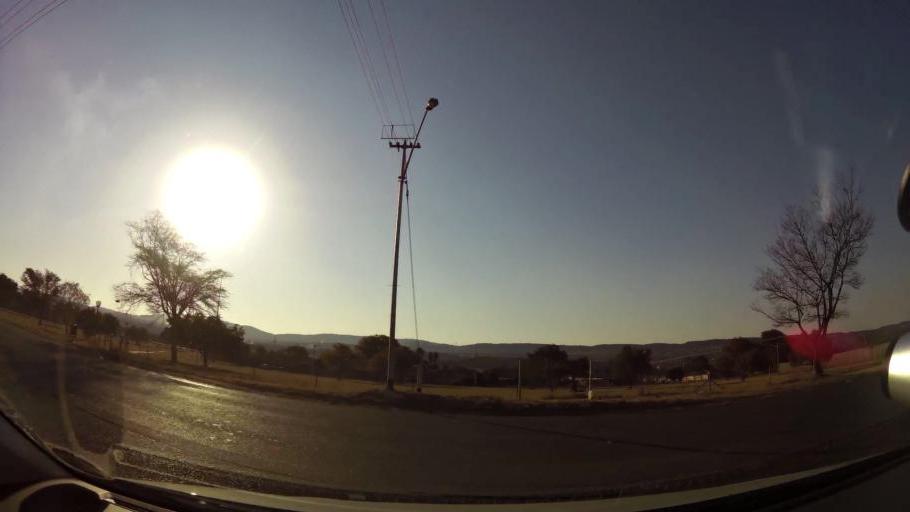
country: ZA
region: Gauteng
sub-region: City of Tshwane Metropolitan Municipality
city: Pretoria
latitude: -25.7558
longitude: 28.1142
